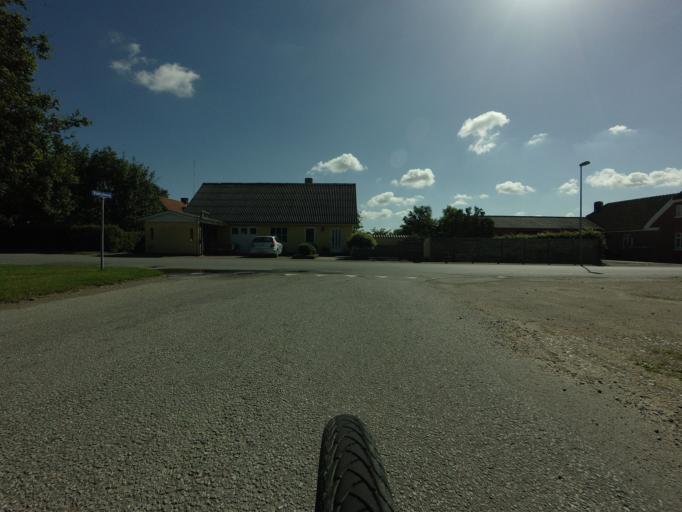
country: DK
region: North Denmark
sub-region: Hjorring Kommune
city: Hjorring
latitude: 57.4335
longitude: 9.9027
